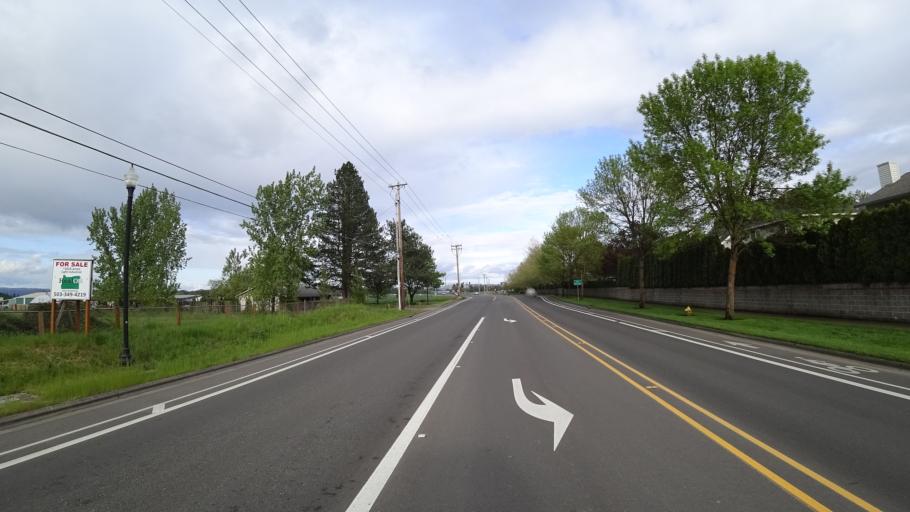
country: US
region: Oregon
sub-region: Washington County
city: Hillsboro
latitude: 45.5500
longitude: -122.9693
